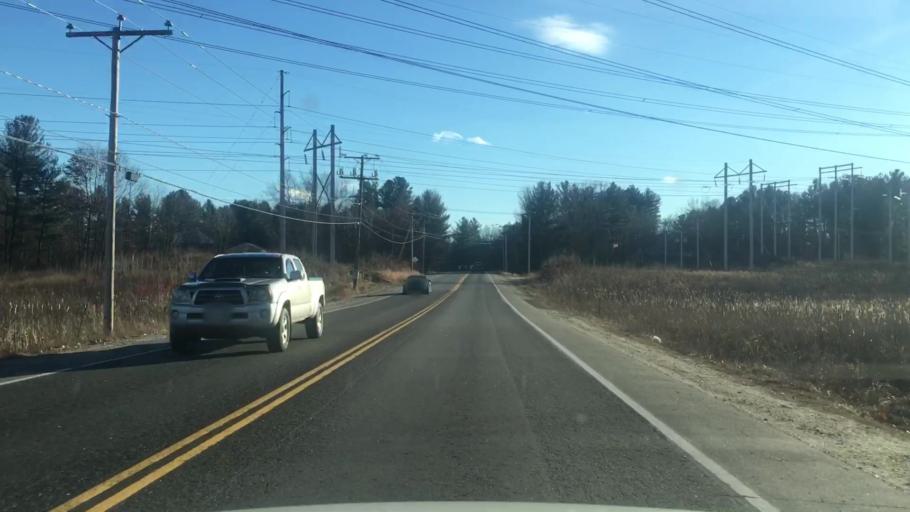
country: US
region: New Hampshire
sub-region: Rockingham County
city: Londonderry
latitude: 42.8812
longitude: -71.3816
